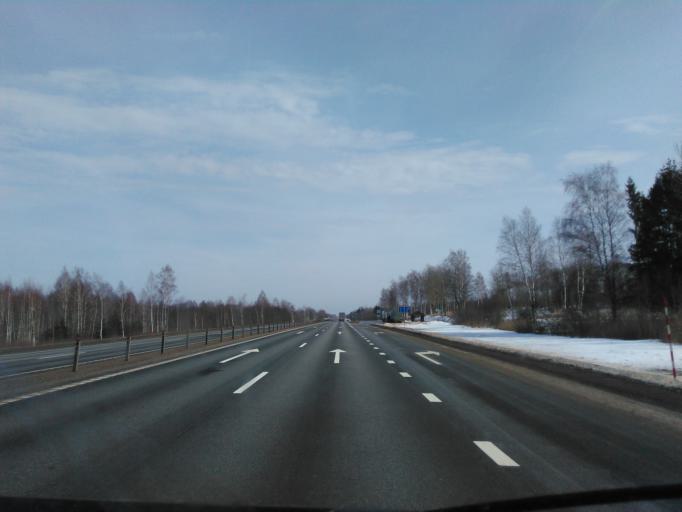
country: BY
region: Vitebsk
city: Dubrowna
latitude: 54.6895
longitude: 30.9014
